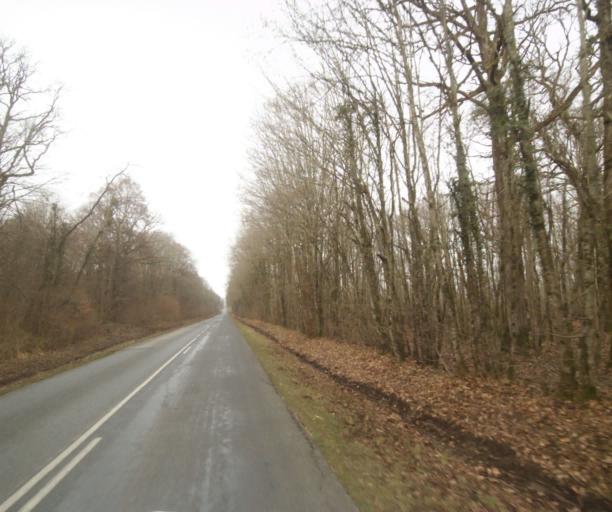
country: FR
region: Champagne-Ardenne
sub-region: Departement de la Haute-Marne
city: Villiers-en-Lieu
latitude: 48.7109
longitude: 4.8876
